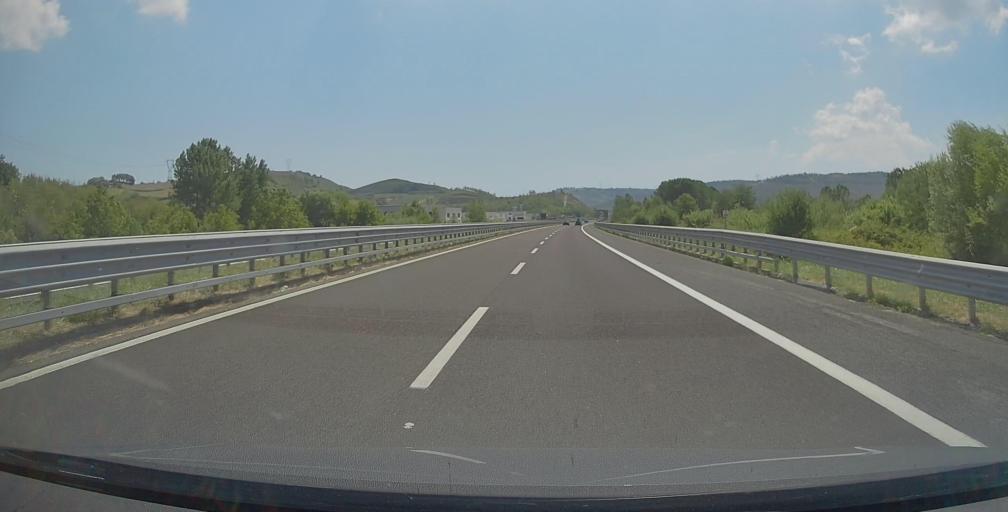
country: IT
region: Calabria
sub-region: Provincia di Vibo-Valentia
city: Soriano Calabro
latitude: 38.6362
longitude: 16.1750
